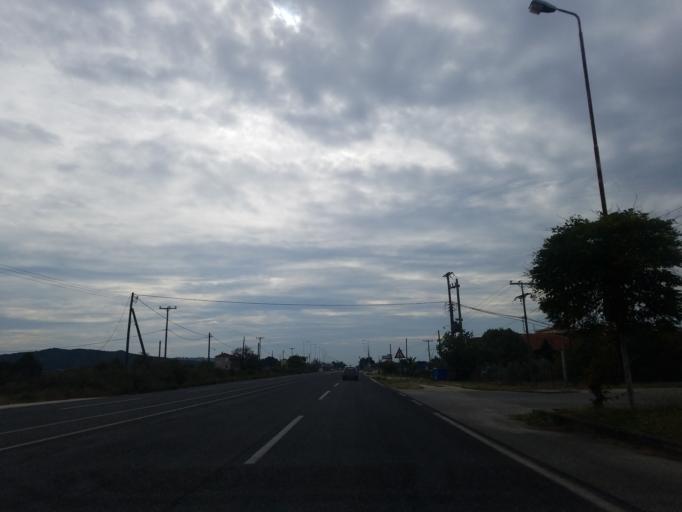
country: GR
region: Thessaly
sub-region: Trikala
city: Kalampaka
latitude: 39.6755
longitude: 21.6603
